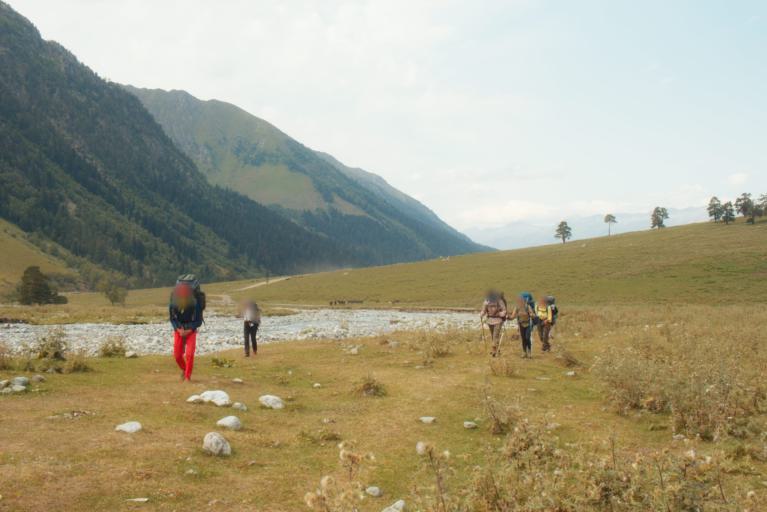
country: RU
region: Karachayevo-Cherkesiya
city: Nizhniy Arkhyz
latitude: 43.4544
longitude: 41.2707
